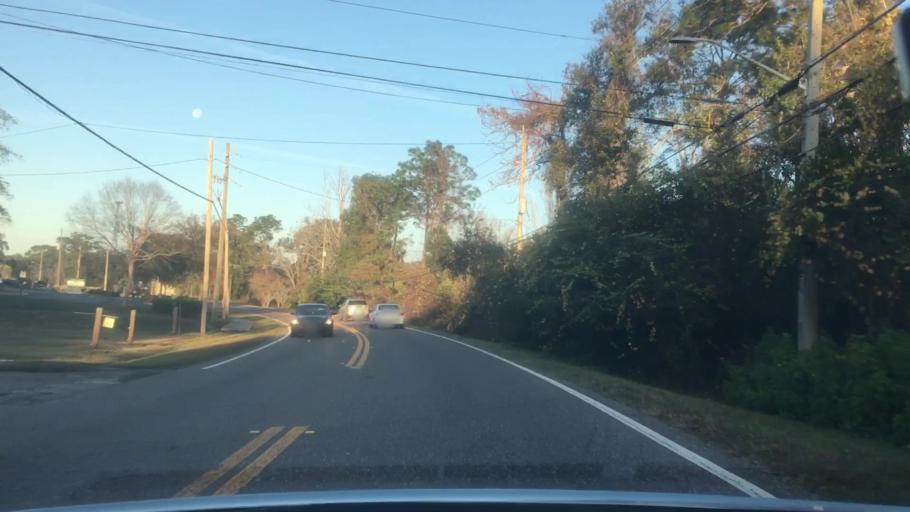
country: US
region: Florida
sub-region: Duval County
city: Jacksonville
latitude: 30.4640
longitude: -81.5830
